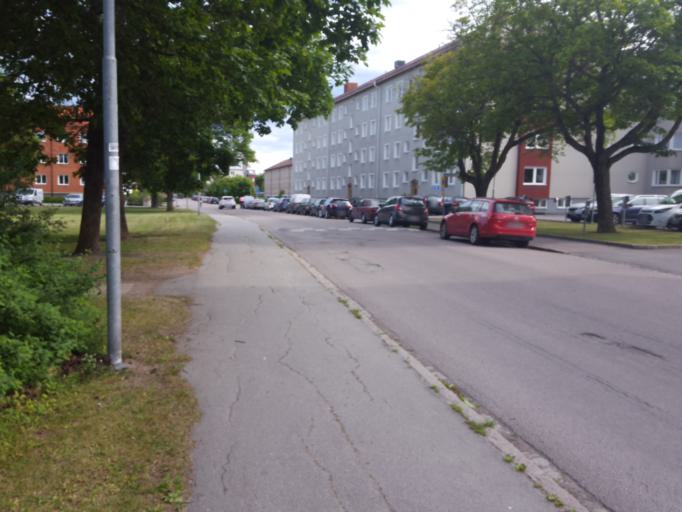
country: SE
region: Uppsala
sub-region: Uppsala Kommun
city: Uppsala
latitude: 59.8654
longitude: 17.6685
